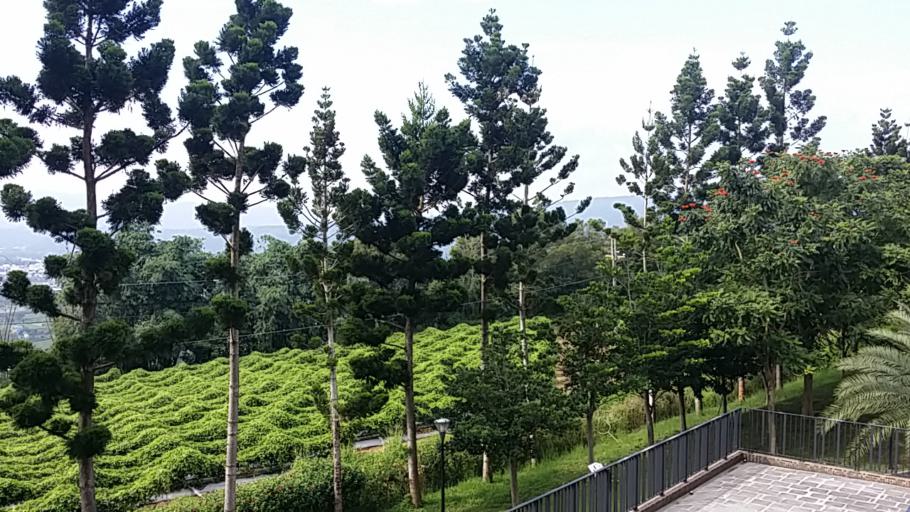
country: TW
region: Taiwan
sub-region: Nantou
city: Puli
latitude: 23.9954
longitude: 120.9387
